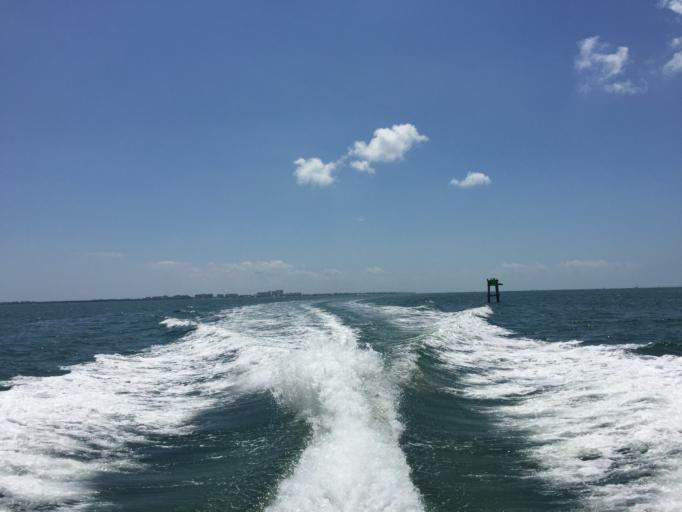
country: US
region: Florida
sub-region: Miami-Dade County
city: Coconut Grove
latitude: 25.7210
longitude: -80.2168
